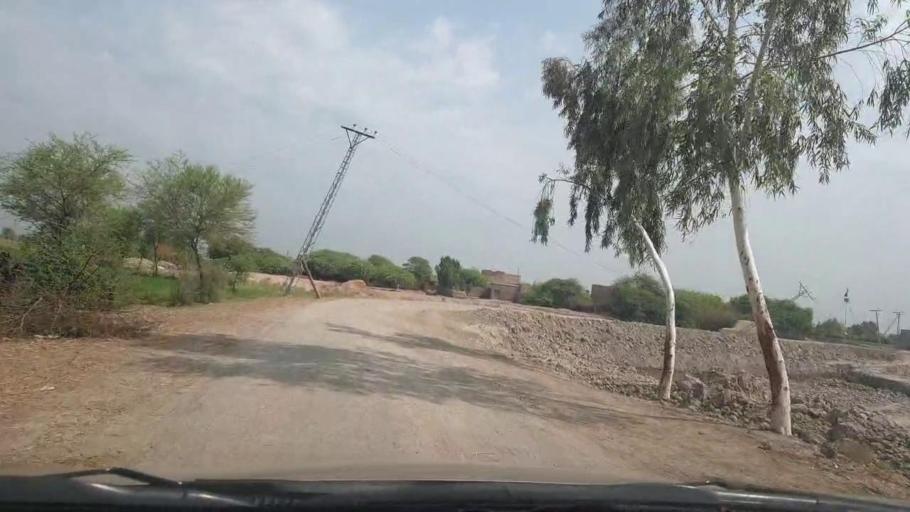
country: PK
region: Sindh
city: Larkana
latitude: 27.6784
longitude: 68.1918
